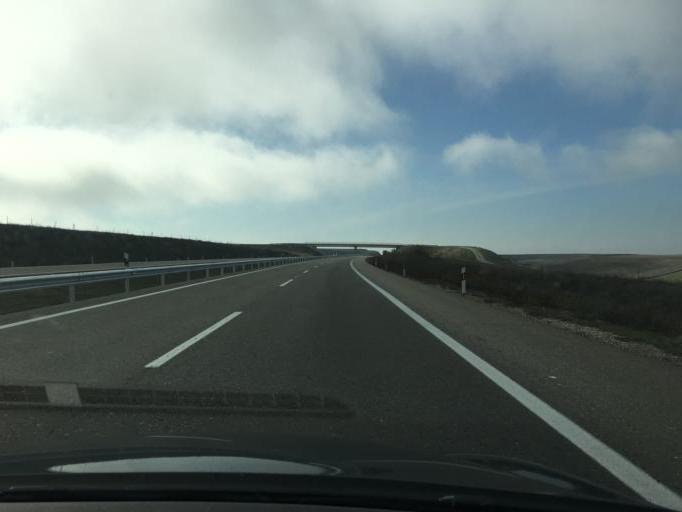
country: ES
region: Castille and Leon
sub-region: Provincia de Burgos
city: Zuneda
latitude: 42.6064
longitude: -3.2099
